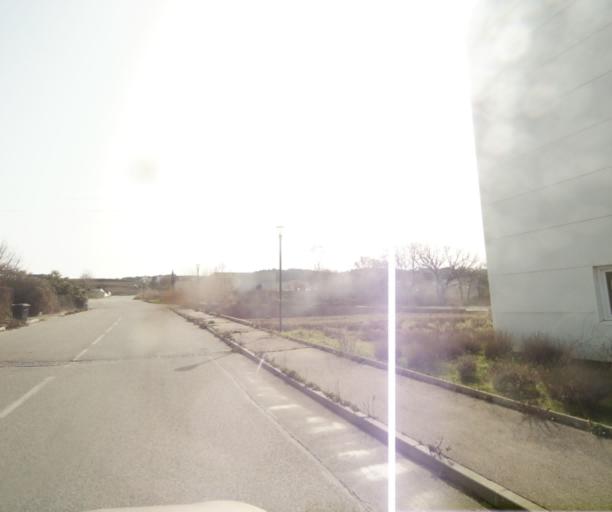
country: FR
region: Provence-Alpes-Cote d'Azur
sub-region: Departement des Bouches-du-Rhone
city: Gardanne
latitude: 43.4647
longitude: 5.4900
